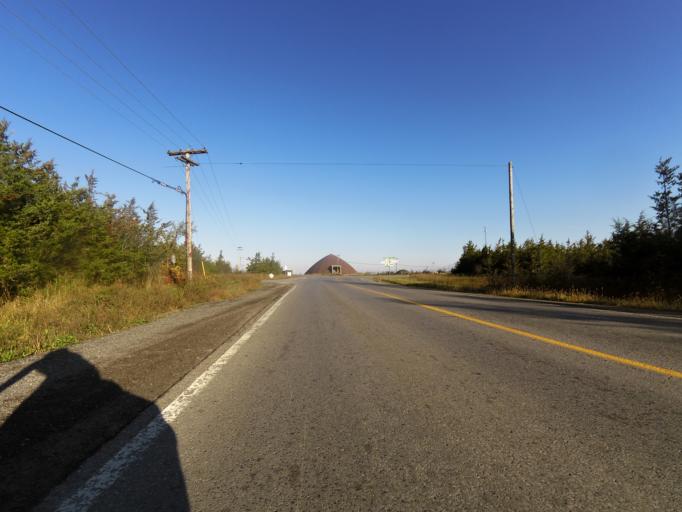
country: CA
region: Ontario
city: Belleville
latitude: 44.0621
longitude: -77.3975
